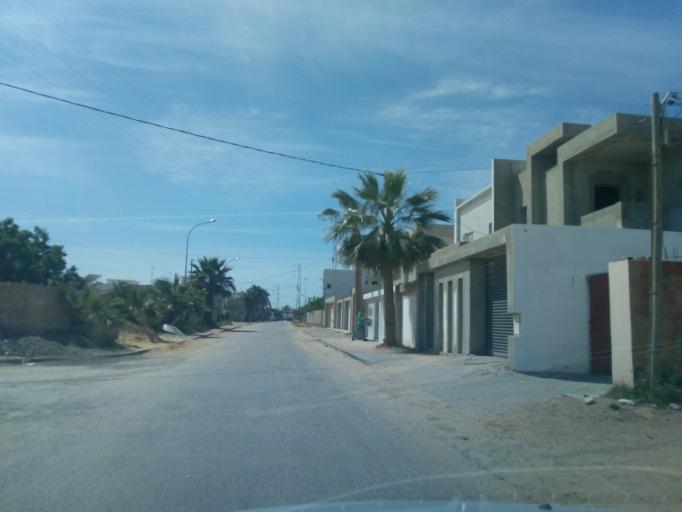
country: TN
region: Safaqis
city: Sfax
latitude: 34.7702
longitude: 10.7007
